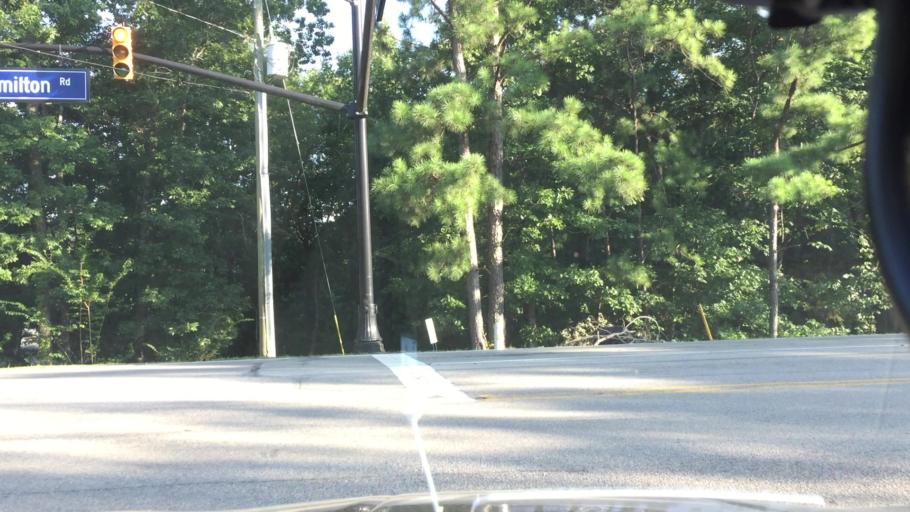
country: US
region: Alabama
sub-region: Lee County
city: Opelika
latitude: 32.5969
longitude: -85.4175
